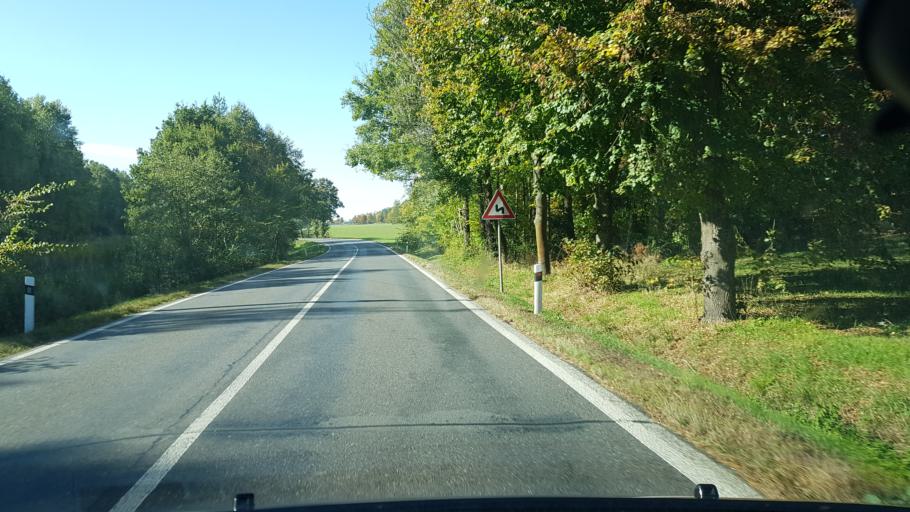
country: CZ
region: Jihocesky
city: Radomysl
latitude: 49.2981
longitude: 14.0083
